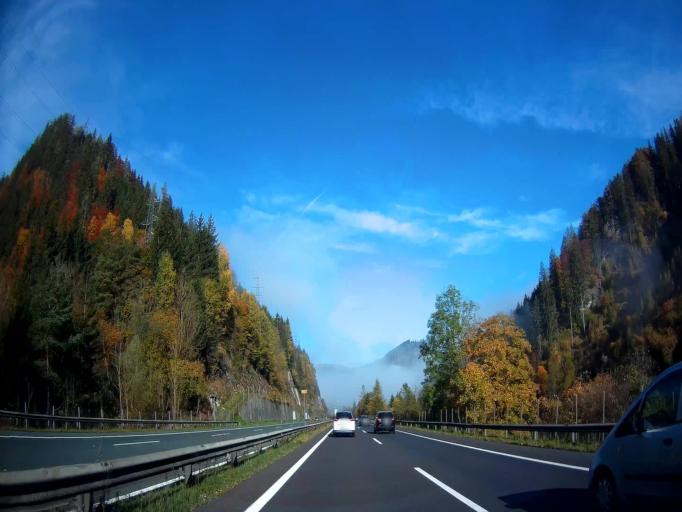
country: AT
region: Styria
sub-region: Politischer Bezirk Leoben
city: Sankt Michael in Obersteiermark
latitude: 47.3085
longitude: 15.0587
